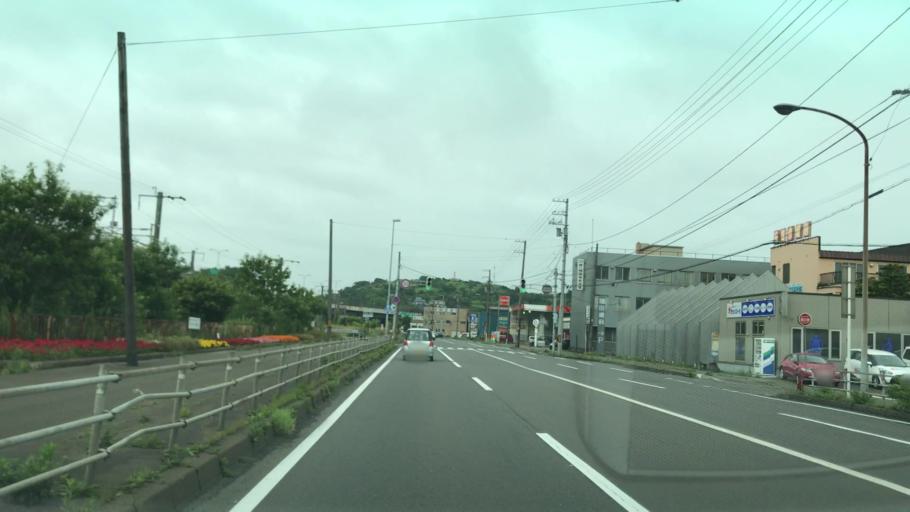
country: JP
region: Hokkaido
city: Muroran
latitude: 42.3359
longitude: 141.0112
